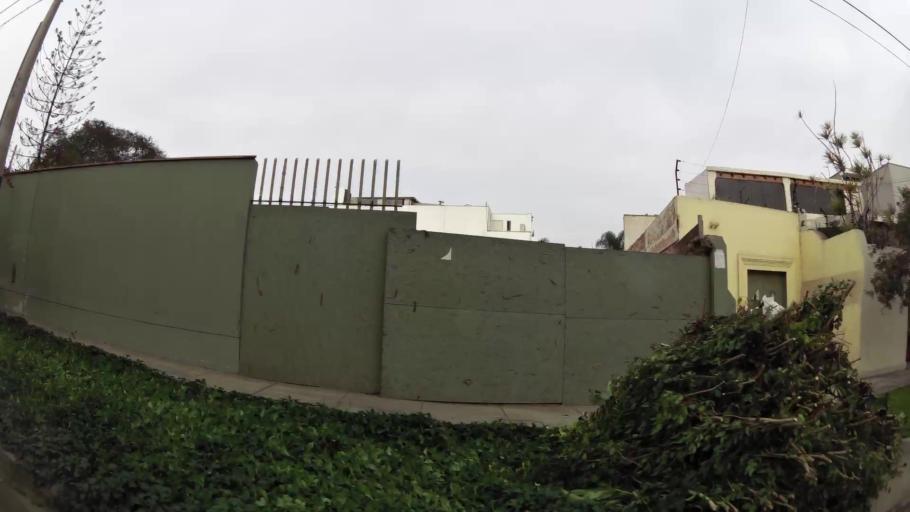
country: PE
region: Lima
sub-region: Lima
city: San Isidro
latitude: -12.1053
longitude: -77.0546
